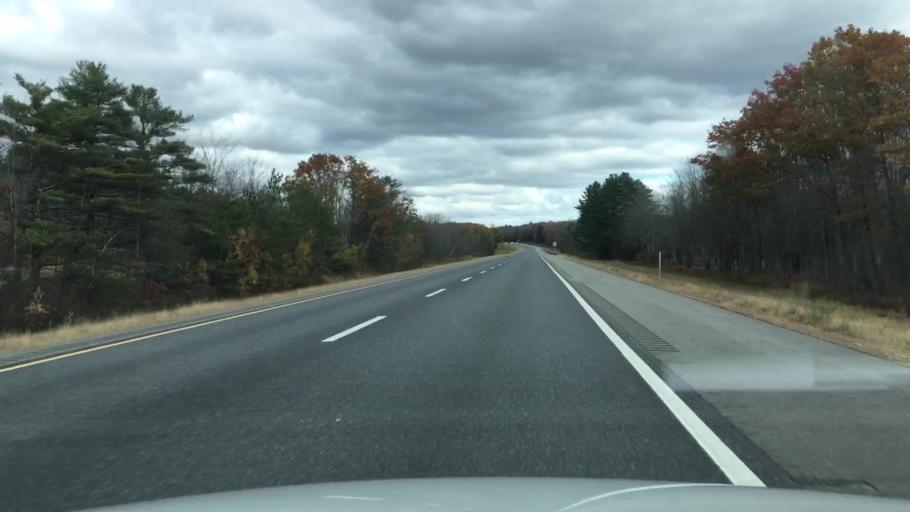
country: US
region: Maine
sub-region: Sagadahoc County
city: Topsham
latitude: 43.9542
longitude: -69.9653
